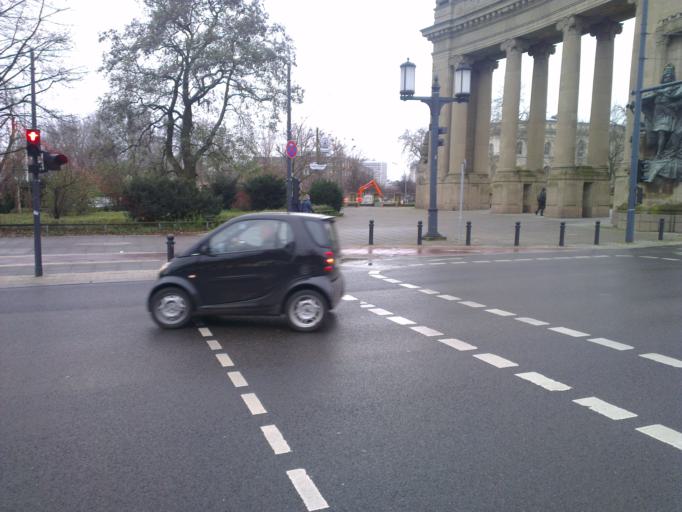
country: DE
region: Berlin
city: Hansaviertel
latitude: 52.5133
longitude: 13.3318
